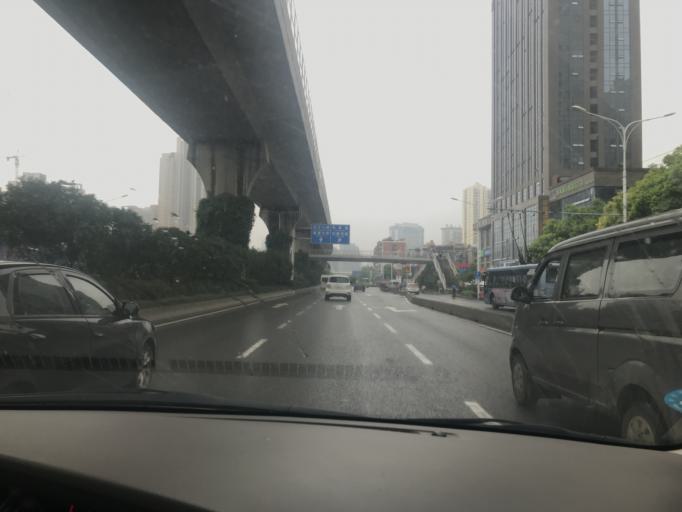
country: CN
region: Hubei
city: Jiang'an
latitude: 30.6246
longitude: 114.3112
